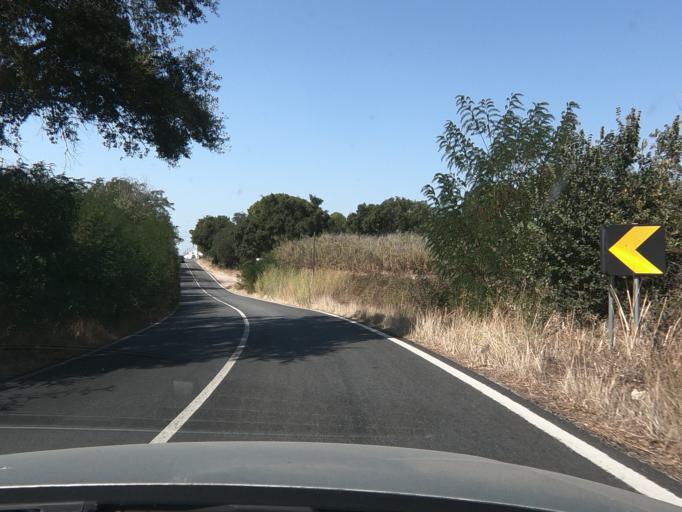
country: PT
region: Setubal
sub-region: Alcacer do Sal
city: Alcacer do Sal
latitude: 38.3615
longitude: -8.4784
